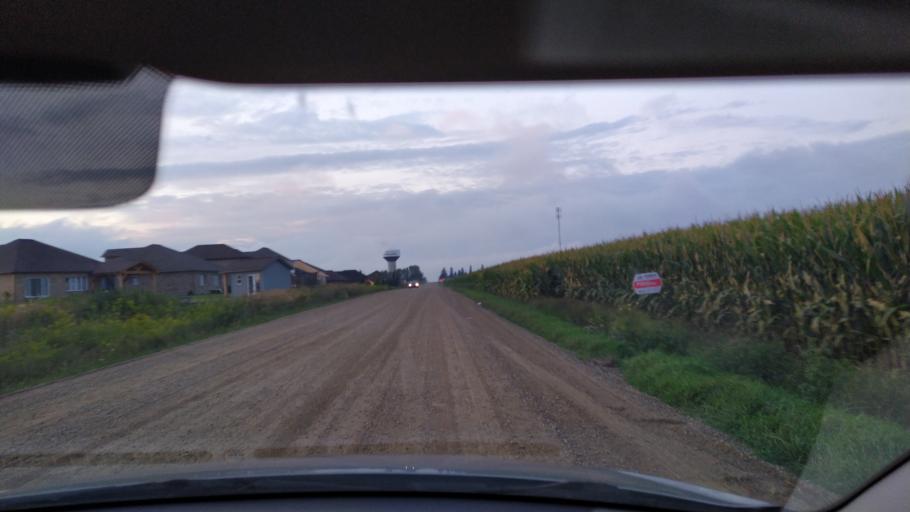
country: CA
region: Ontario
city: Kitchener
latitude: 43.3060
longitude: -80.6096
